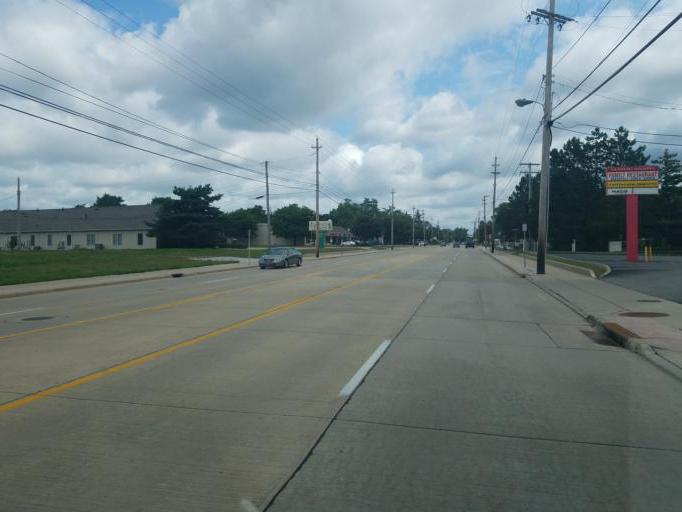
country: US
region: Ohio
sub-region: Lake County
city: Painesville
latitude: 41.6909
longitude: -81.2869
